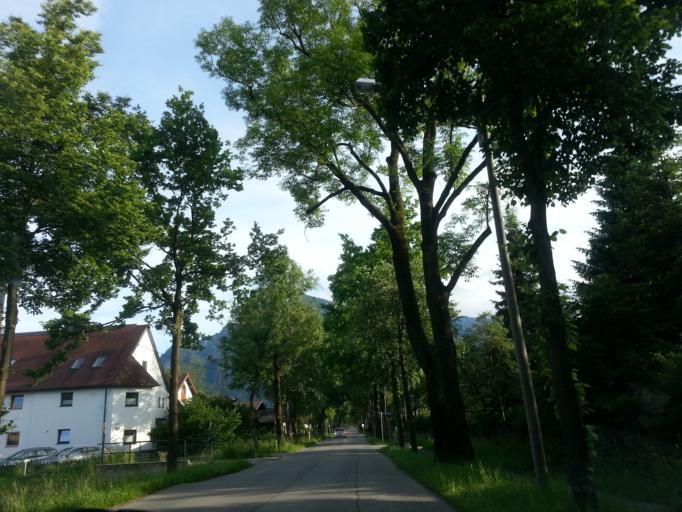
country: AT
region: Salzburg
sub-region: Salzburg Stadt
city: Salzburg
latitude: 47.7721
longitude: 13.0210
